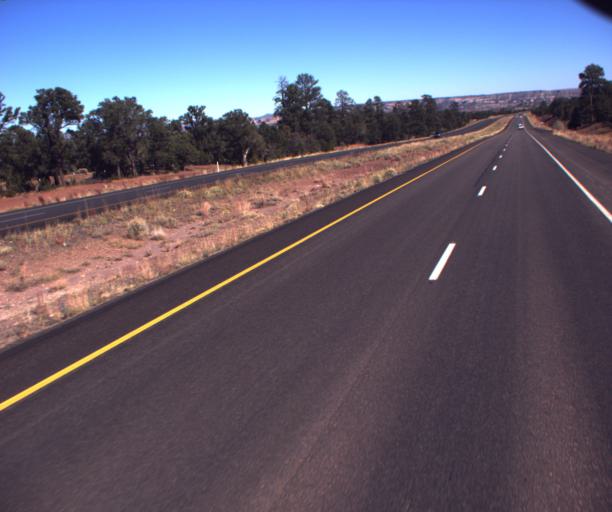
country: US
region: Arizona
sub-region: Apache County
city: Saint Michaels
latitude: 35.6580
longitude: -109.1346
